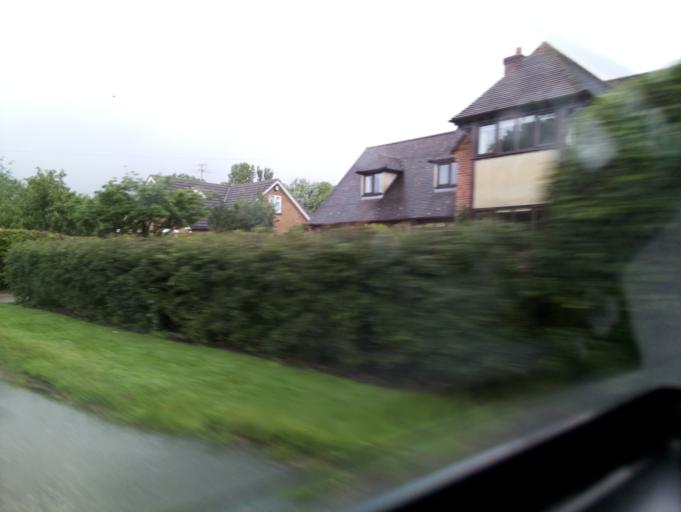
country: GB
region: England
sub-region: Gloucestershire
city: Tewkesbury
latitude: 51.9642
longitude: -2.1413
